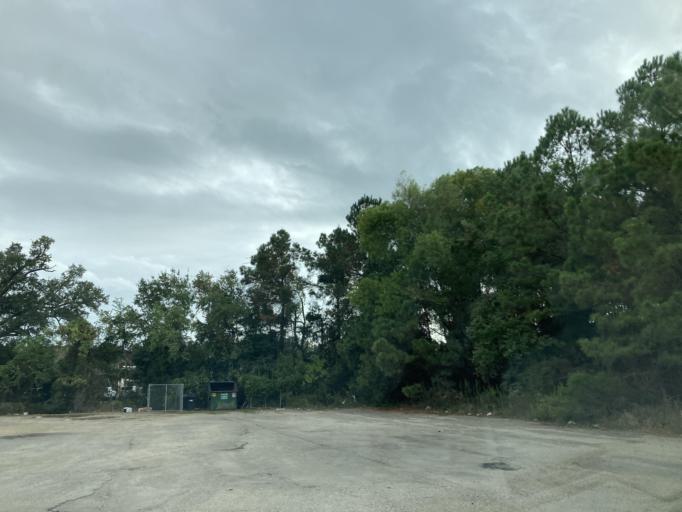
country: US
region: Mississippi
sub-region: Jackson County
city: Gulf Hills
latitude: 30.4298
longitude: -88.8300
